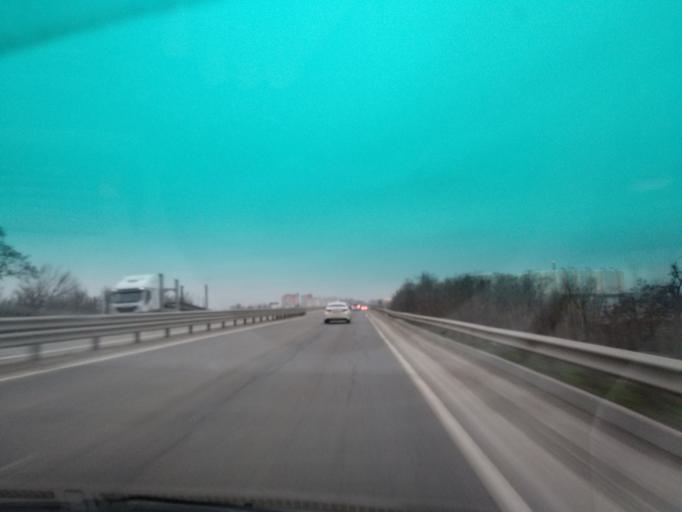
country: RU
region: Krasnodarskiy
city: Pashkovskiy
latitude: 45.0459
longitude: 39.1290
